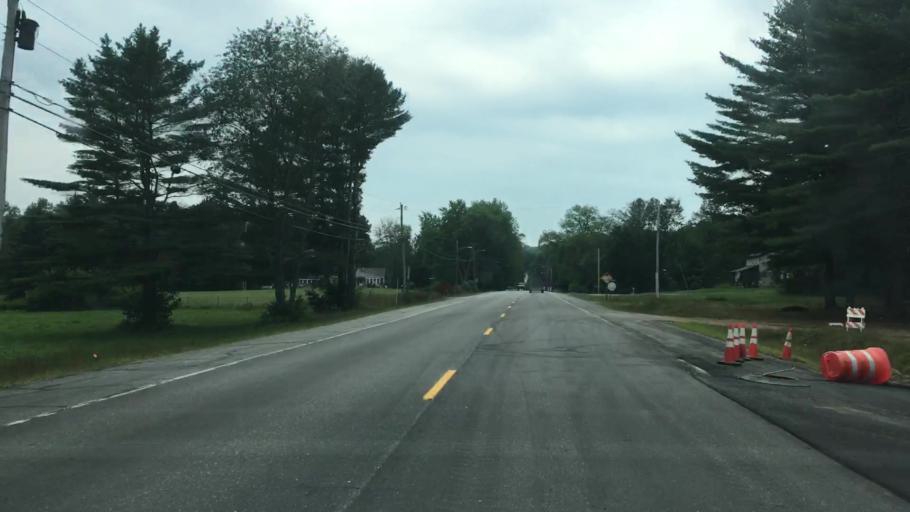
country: US
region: Maine
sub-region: Oxford County
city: Bethel
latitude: 44.5010
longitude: -70.6875
